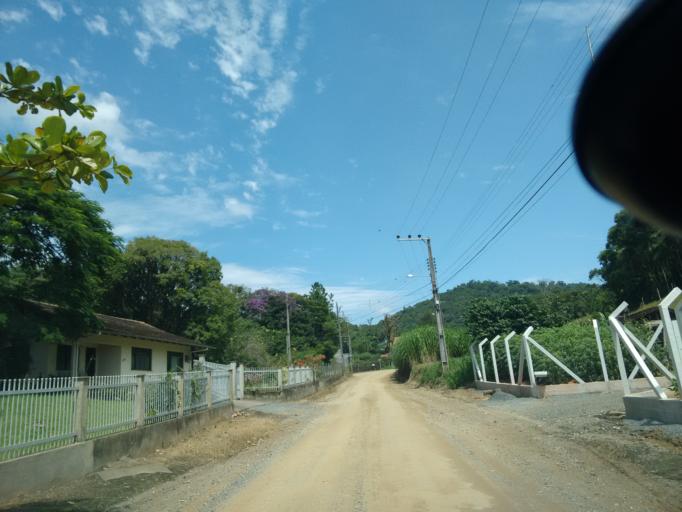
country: BR
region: Santa Catarina
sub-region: Indaial
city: Indaial
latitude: -26.8494
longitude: -49.1606
